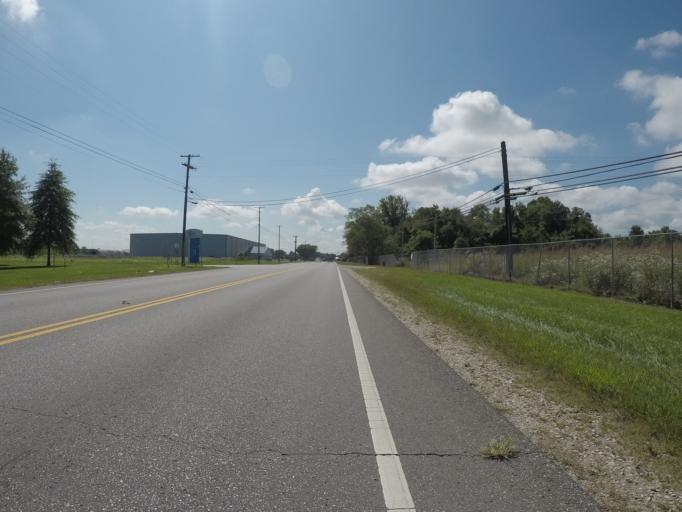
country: US
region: Ohio
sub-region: Lawrence County
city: South Point
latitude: 38.4364
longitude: -82.5948
